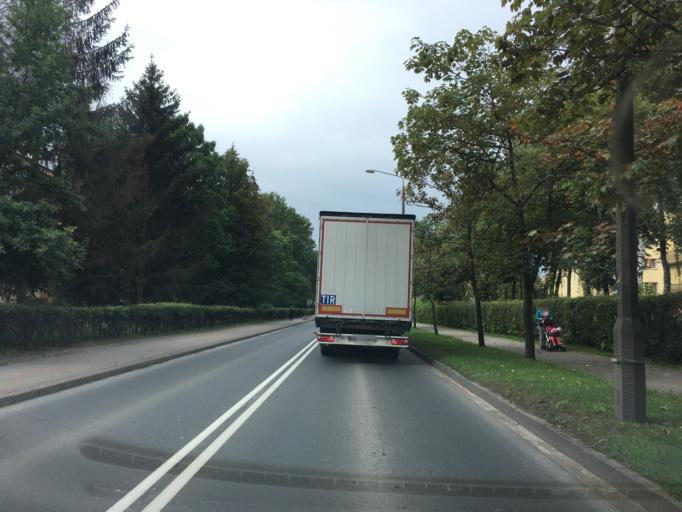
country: PL
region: Warmian-Masurian Voivodeship
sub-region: Powiat ostrodzki
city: Ostroda
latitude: 53.6935
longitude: 19.9715
